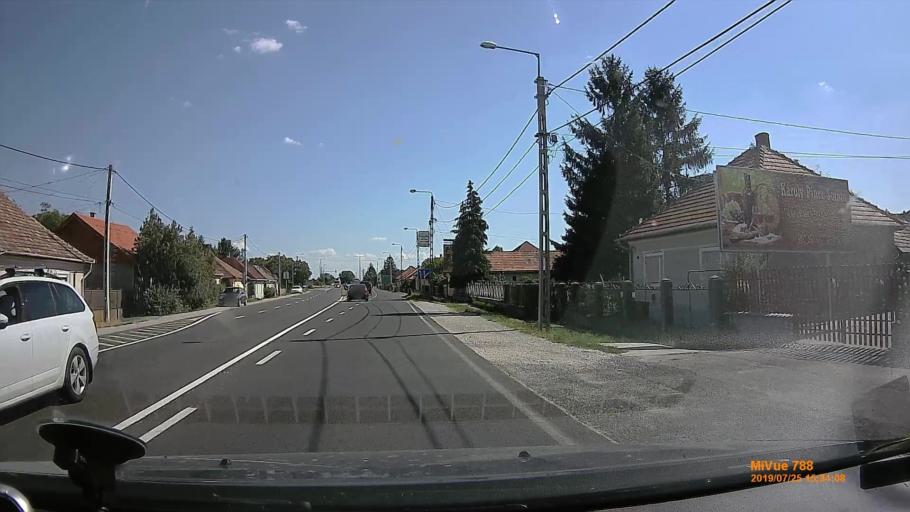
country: HU
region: Borsod-Abauj-Zemplen
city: Nyekladhaza
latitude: 47.9896
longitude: 20.8307
